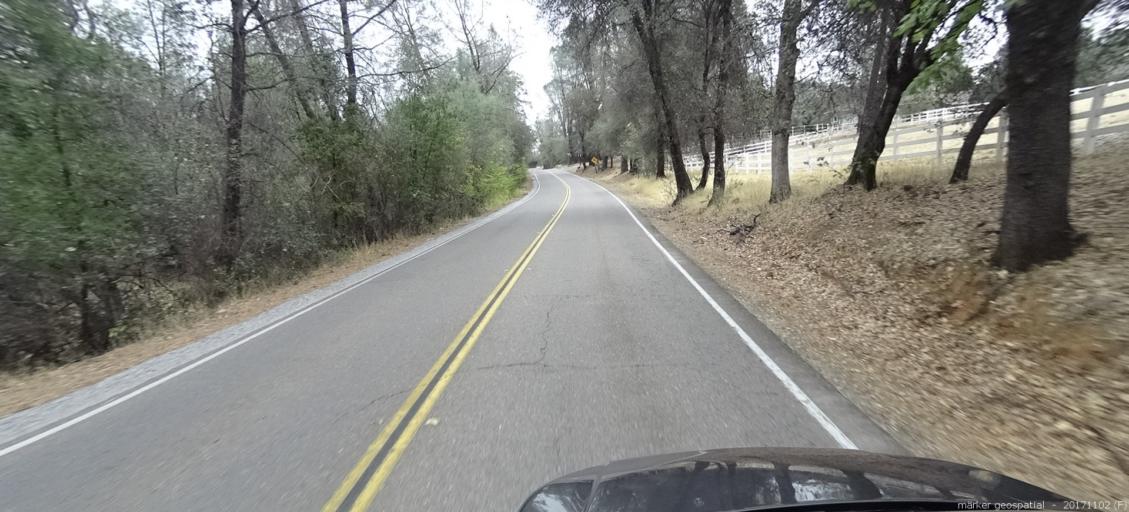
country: US
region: California
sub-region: Shasta County
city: Shasta Lake
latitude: 40.6800
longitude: -122.2999
